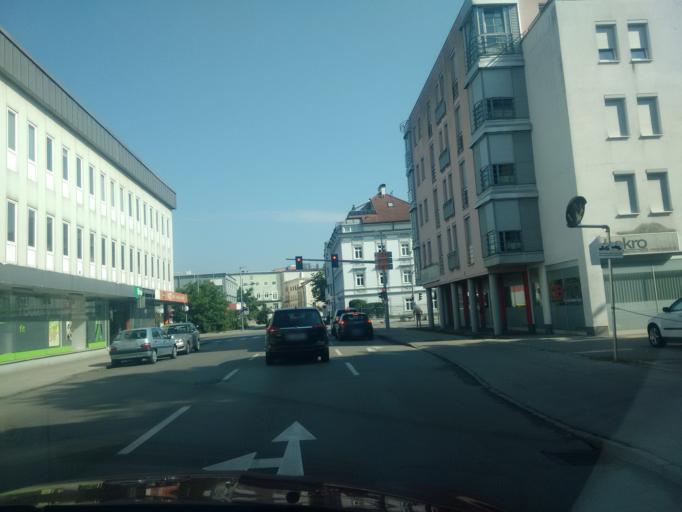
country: AT
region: Upper Austria
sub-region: Wels-Land
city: Thalheim bei Wels
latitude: 48.1546
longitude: 14.0264
